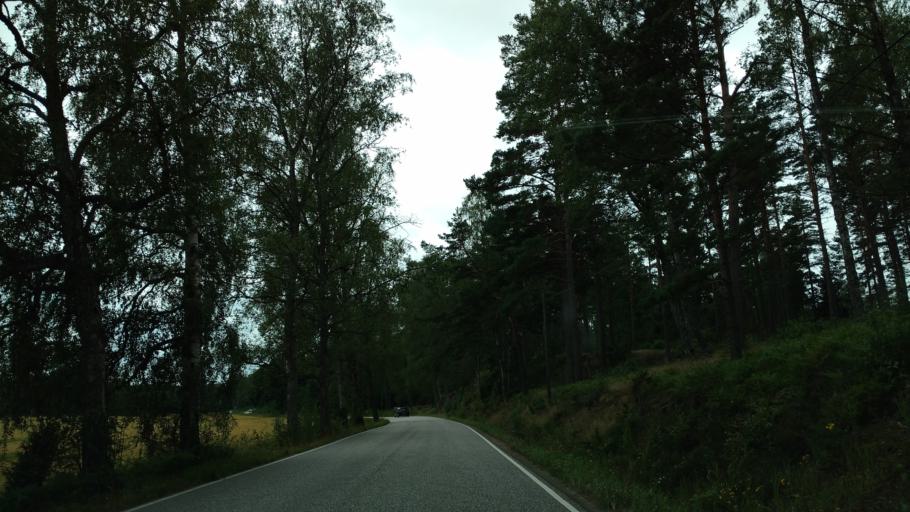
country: FI
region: Varsinais-Suomi
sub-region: Aboland-Turunmaa
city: Dragsfjaerd
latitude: 60.0385
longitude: 22.4428
